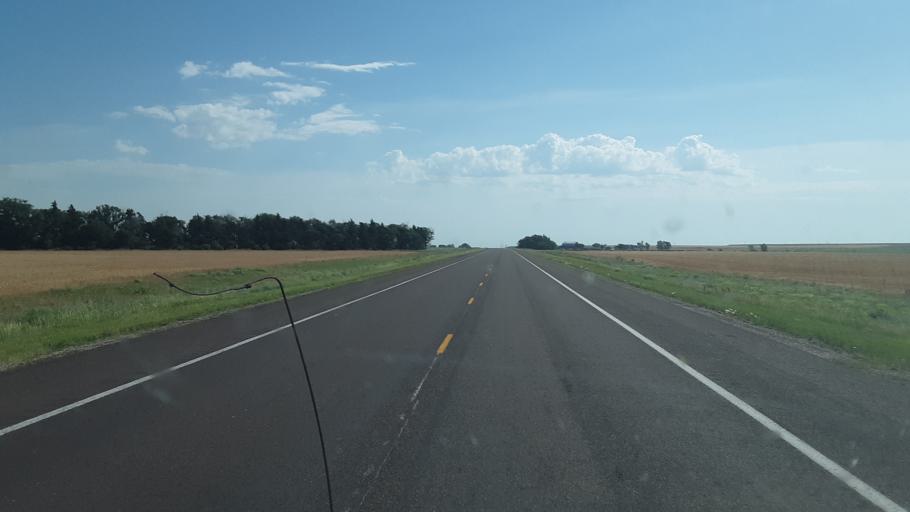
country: US
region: Kansas
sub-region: Ellsworth County
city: Ellsworth
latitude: 38.6272
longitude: -98.3599
